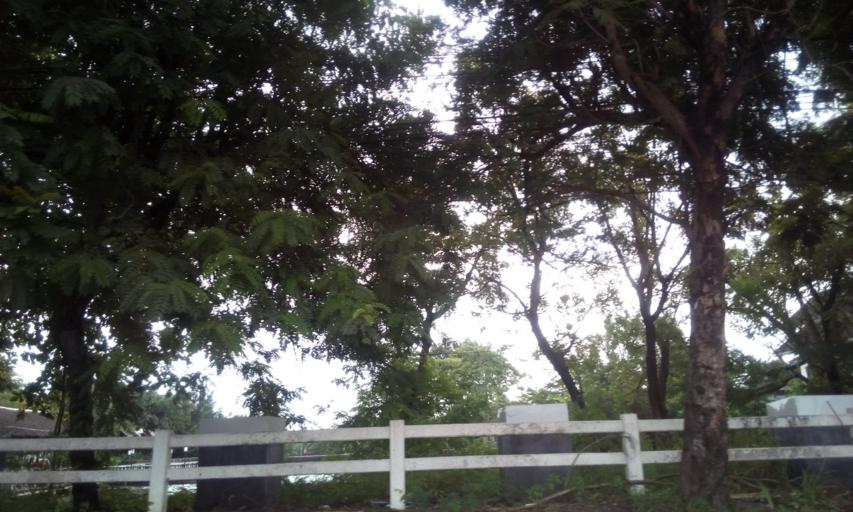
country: TH
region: Bangkok
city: Don Mueang
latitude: 13.9347
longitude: 100.5624
